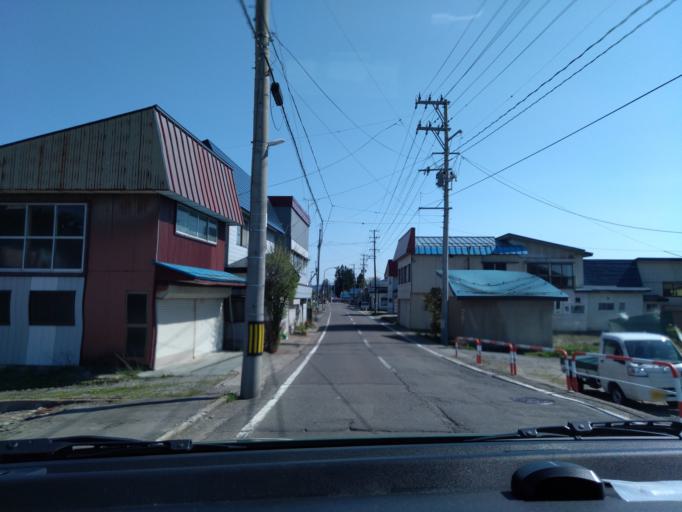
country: JP
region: Akita
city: Kakunodatemachi
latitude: 39.4966
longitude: 140.5940
